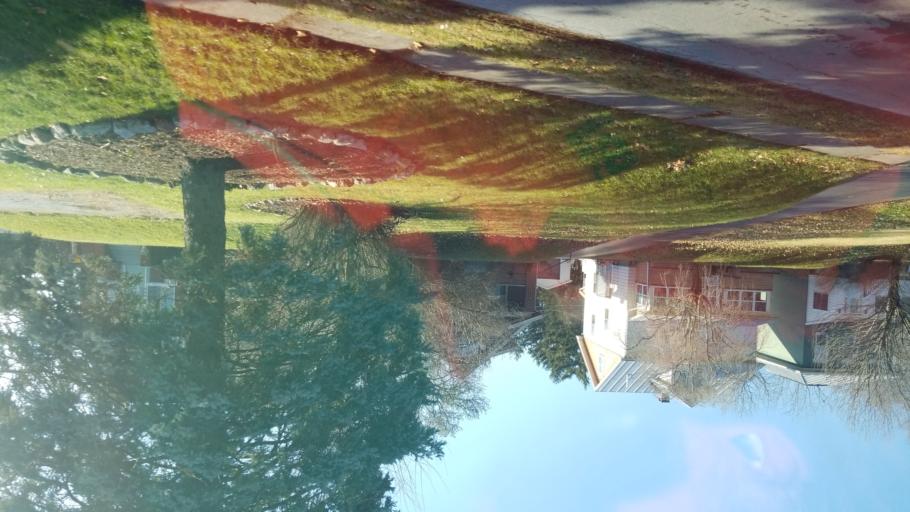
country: US
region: Ohio
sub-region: Seneca County
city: Tiffin
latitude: 41.1184
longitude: -83.1747
